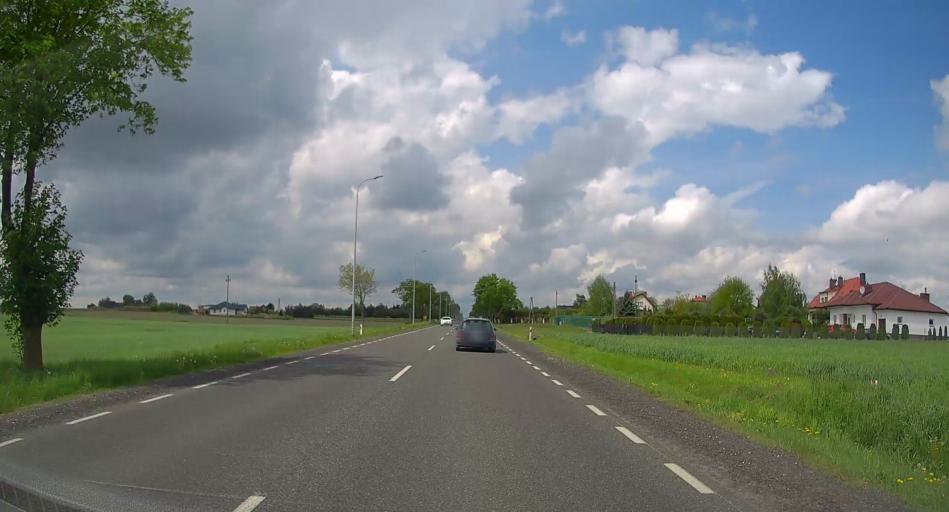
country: PL
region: Masovian Voivodeship
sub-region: Powiat plonski
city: Zaluski
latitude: 52.4432
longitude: 20.5341
